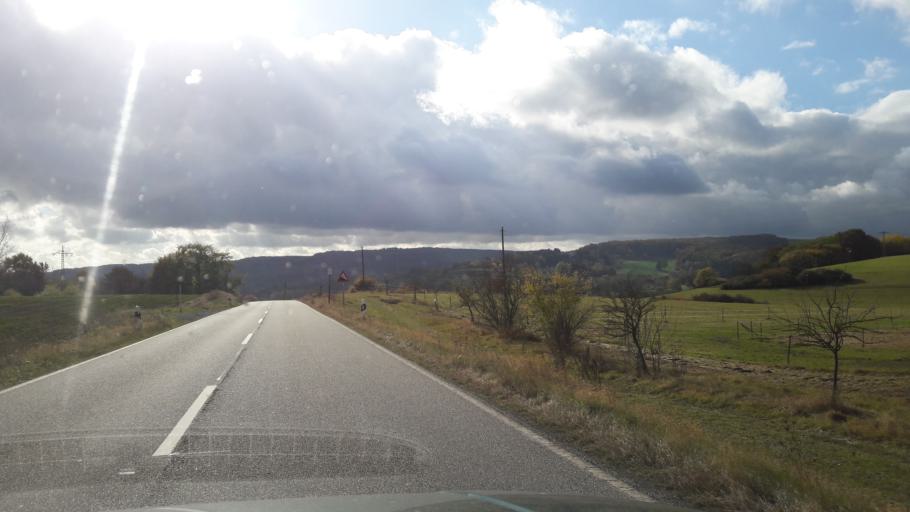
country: DE
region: Rheinland-Pfalz
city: Krottelbach
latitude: 49.4560
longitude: 7.3255
